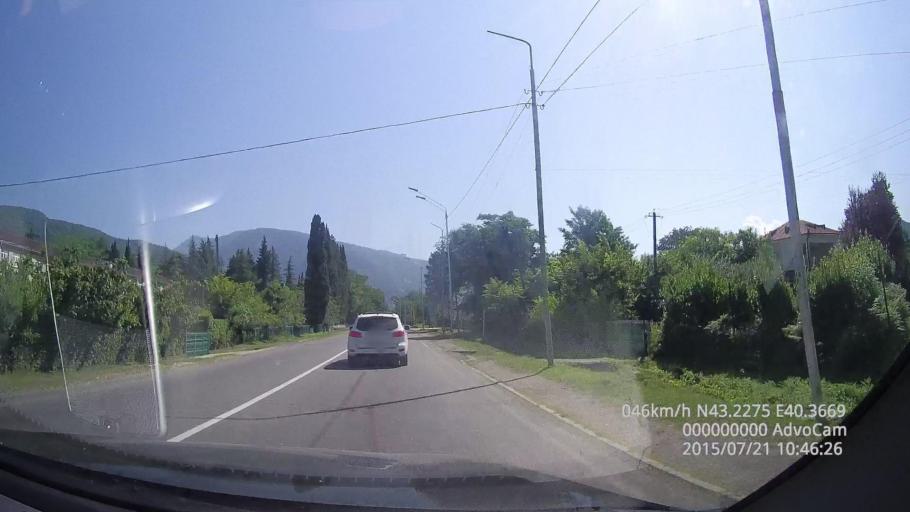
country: GE
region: Abkhazia
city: Bich'vinta
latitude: 43.2276
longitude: 40.3671
